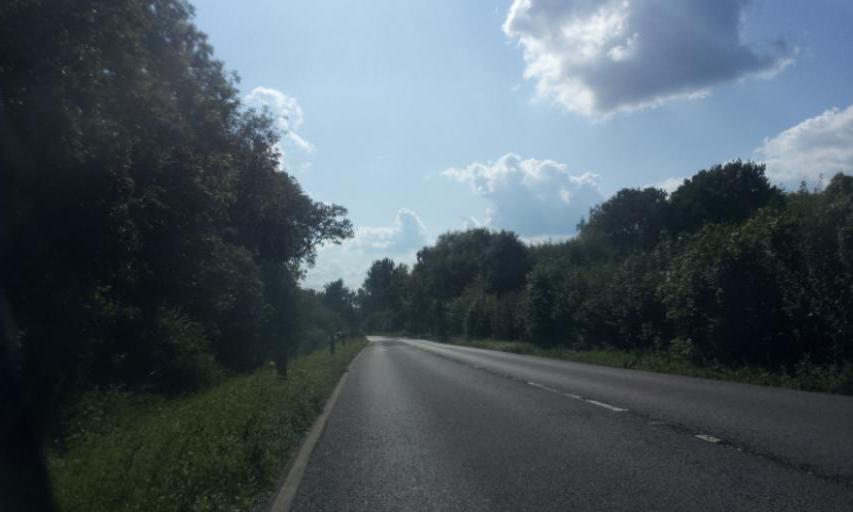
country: GB
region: England
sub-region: Kent
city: East Peckham
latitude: 51.2288
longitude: 0.4032
